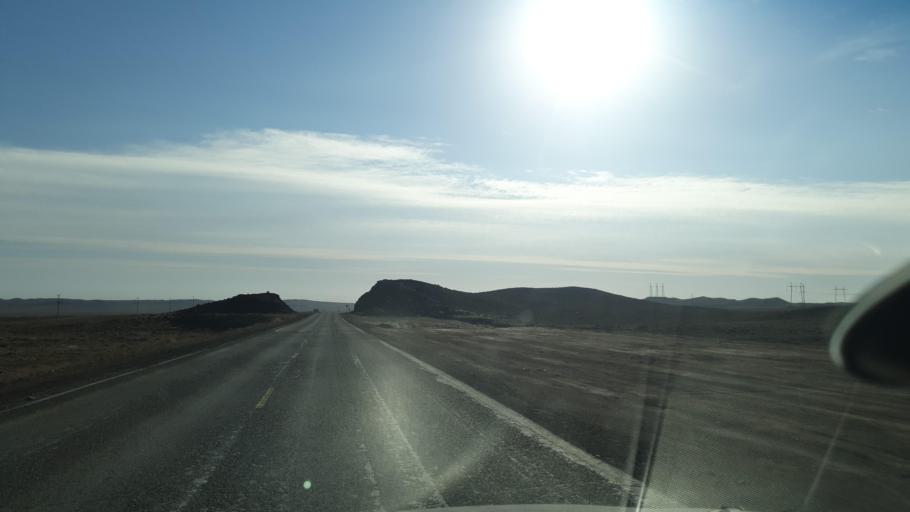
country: KZ
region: Zhambyl
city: Mynaral
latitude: 45.6964
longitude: 73.3997
